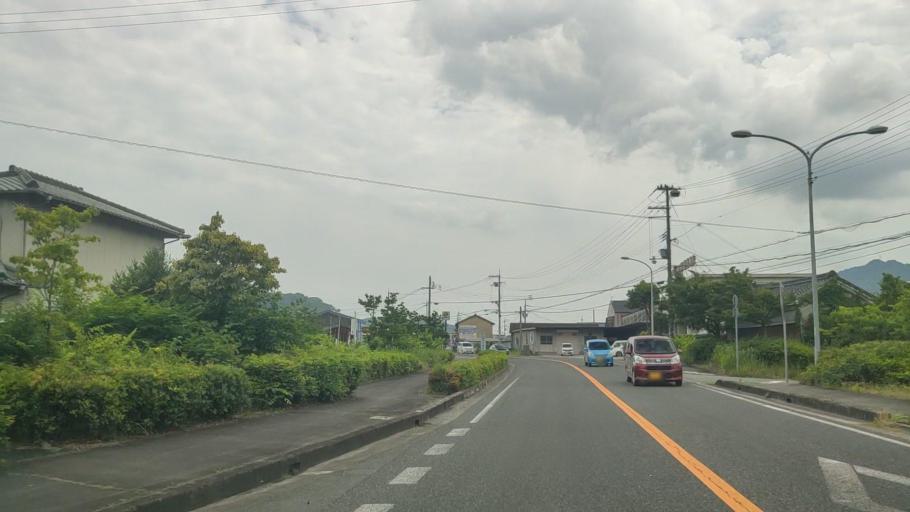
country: JP
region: Hyogo
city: Tatsunocho-tominaga
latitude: 34.9125
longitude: 134.5496
